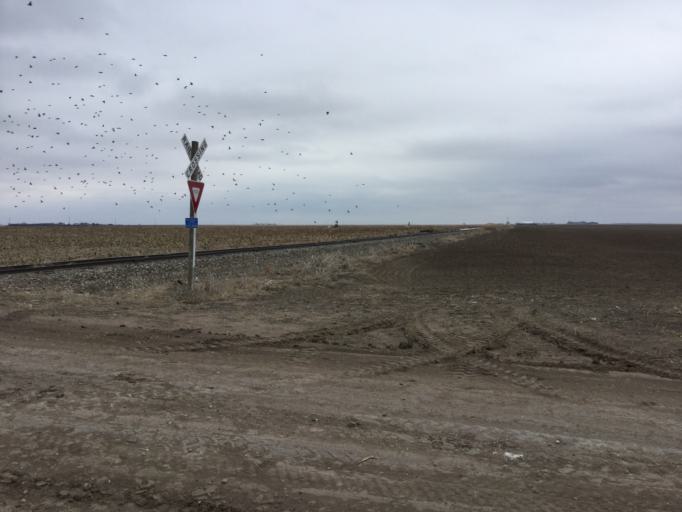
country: US
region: Kansas
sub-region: Scott County
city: Scott City
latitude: 38.4856
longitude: -100.7601
